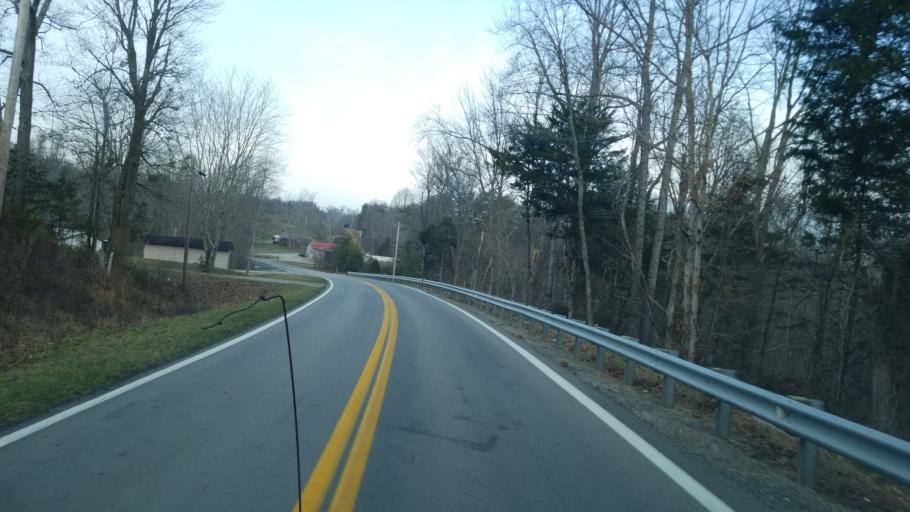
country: US
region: Kentucky
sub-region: Clinton County
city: Albany
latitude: 36.8258
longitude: -85.1918
